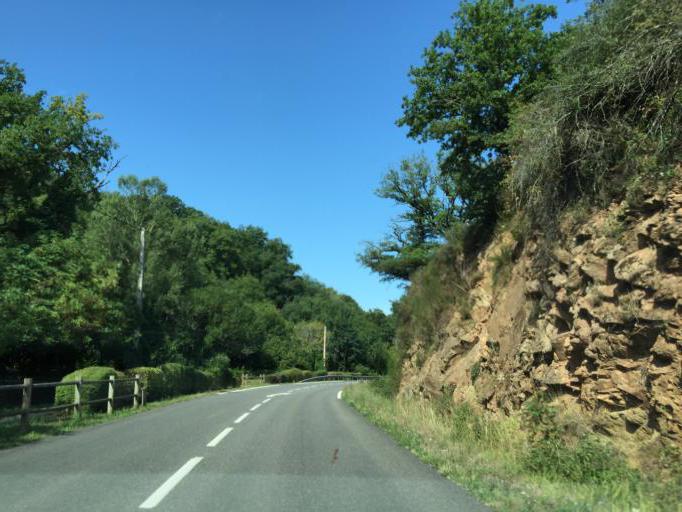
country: FR
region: Midi-Pyrenees
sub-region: Departement de l'Aveyron
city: Le Monastere
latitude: 44.3348
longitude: 2.5910
